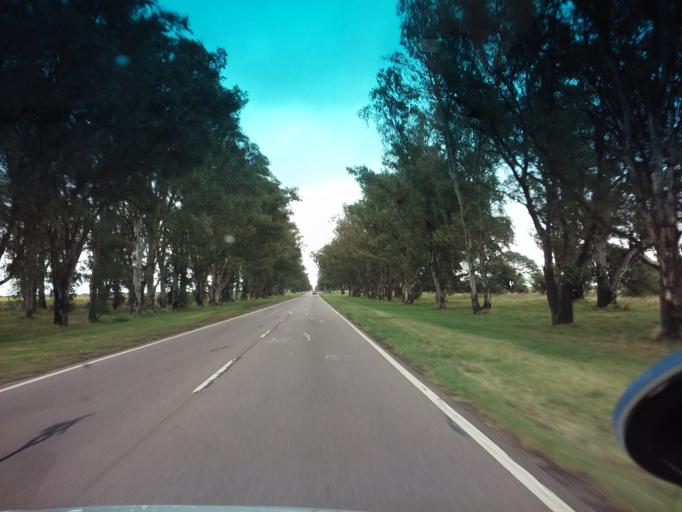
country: AR
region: La Pampa
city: Anguil
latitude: -36.5704
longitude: -64.1441
